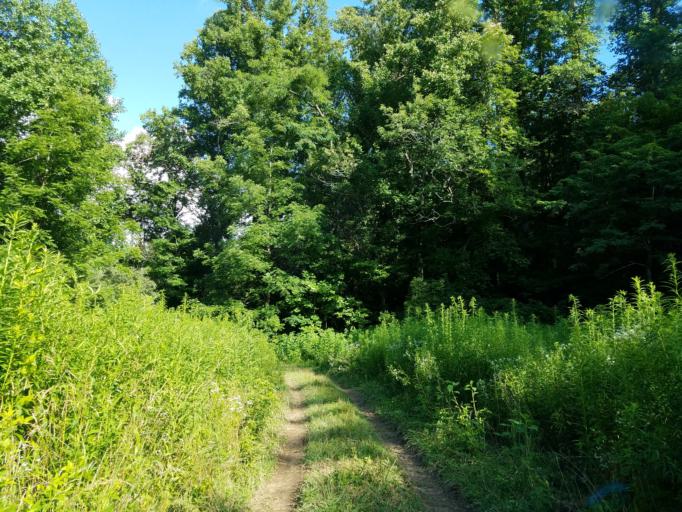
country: US
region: Georgia
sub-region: Lumpkin County
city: Dahlonega
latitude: 34.6876
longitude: -84.0548
